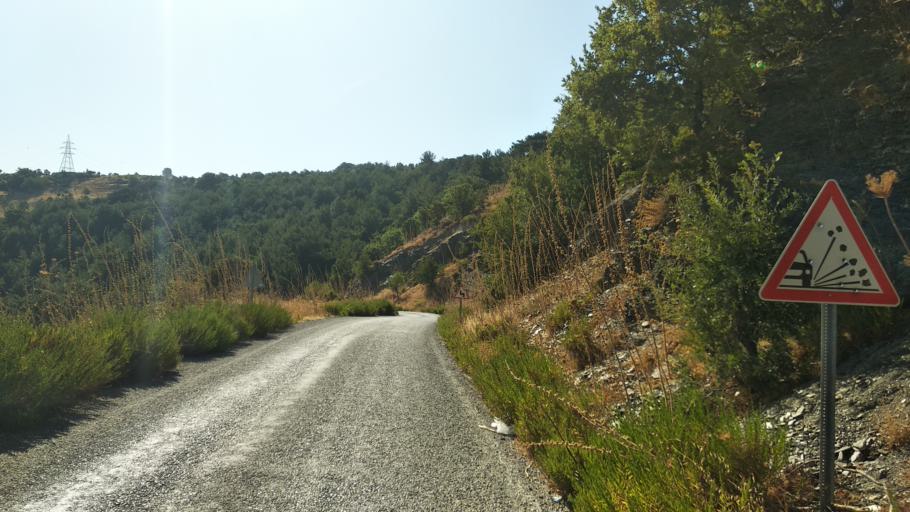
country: TR
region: Izmir
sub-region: Seferihisar
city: Seferhisar
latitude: 38.3297
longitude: 26.9462
